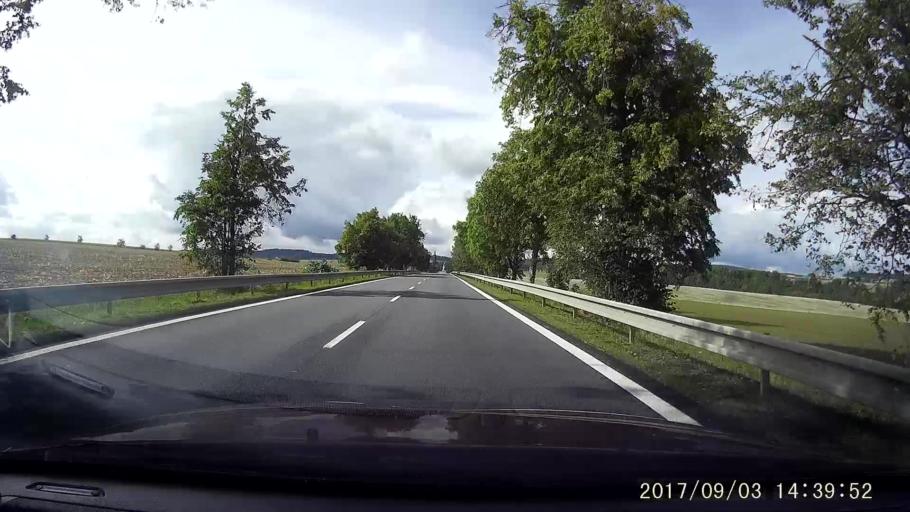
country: CZ
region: Vysocina
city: Moravske Budejovice
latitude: 49.0900
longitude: 15.7463
